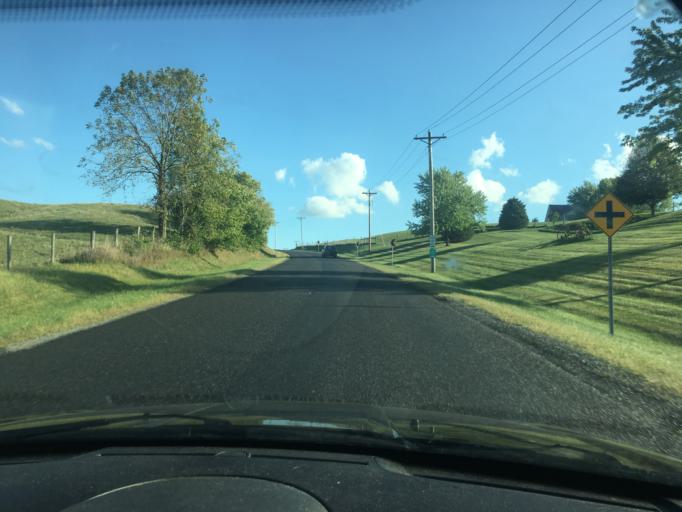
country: US
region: Ohio
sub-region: Logan County
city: West Liberty
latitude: 40.2717
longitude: -83.7231
